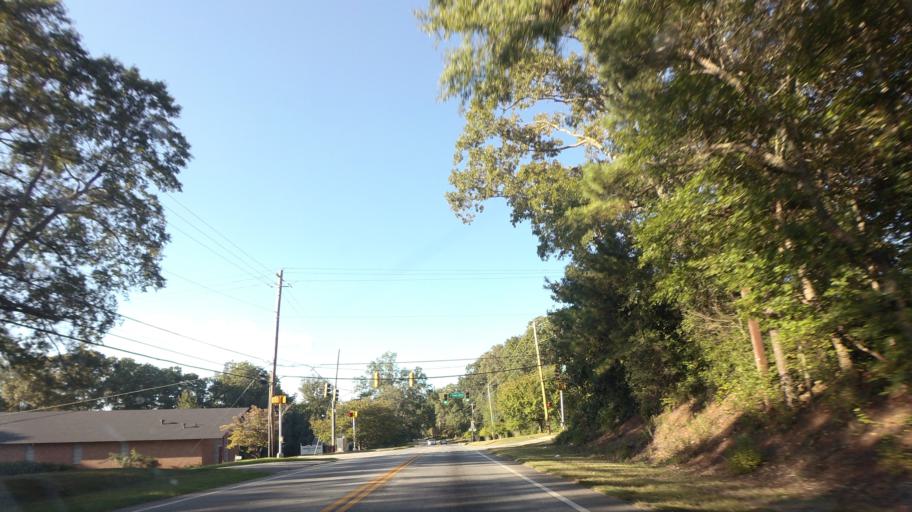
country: US
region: Georgia
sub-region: Spalding County
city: Griffin
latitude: 33.2361
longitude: -84.2643
